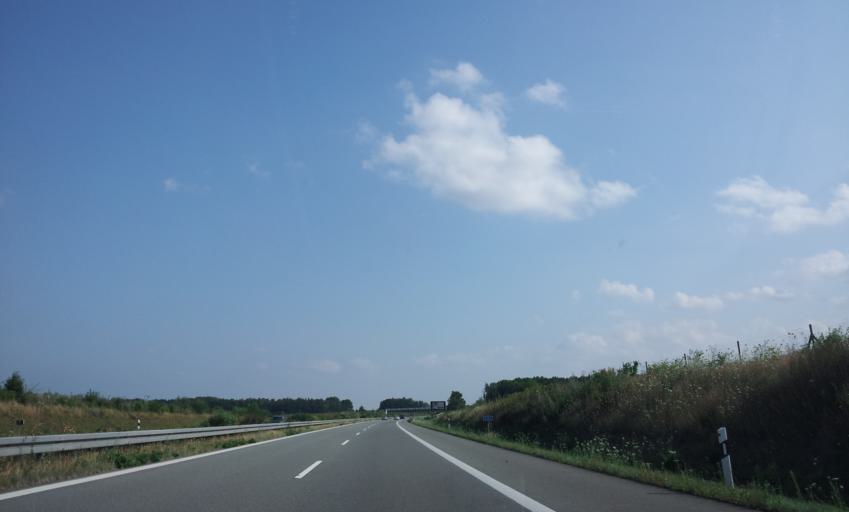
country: DE
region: Mecklenburg-Vorpommern
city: Jarmen
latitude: 53.9691
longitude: 13.3635
